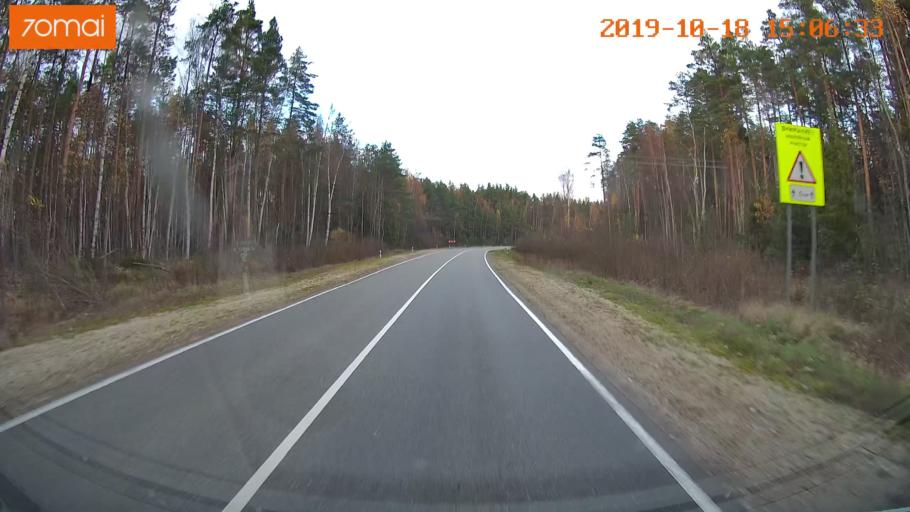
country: RU
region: Vladimir
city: Gus'-Khrustal'nyy
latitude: 55.5318
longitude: 40.5795
